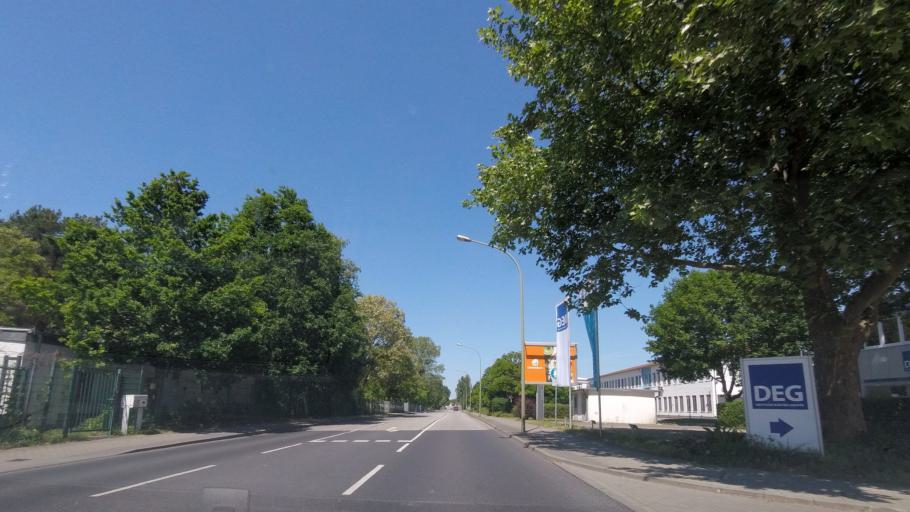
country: DE
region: Brandenburg
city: Potsdam
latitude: 52.3558
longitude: 13.1151
